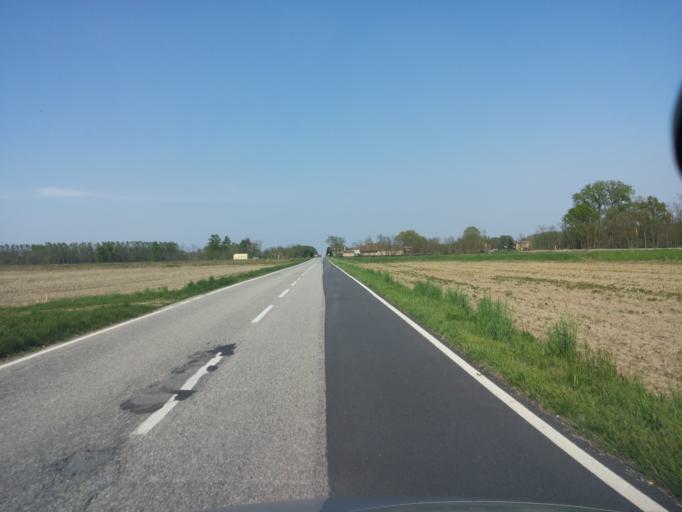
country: IT
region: Lombardy
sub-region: Provincia di Pavia
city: Zeme
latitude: 45.2078
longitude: 8.6430
